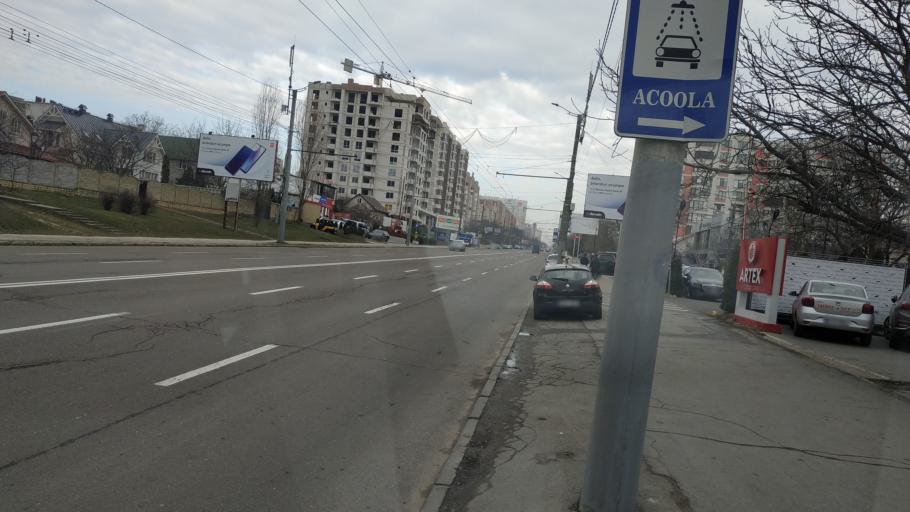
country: MD
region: Chisinau
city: Vatra
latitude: 47.0331
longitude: 28.7808
